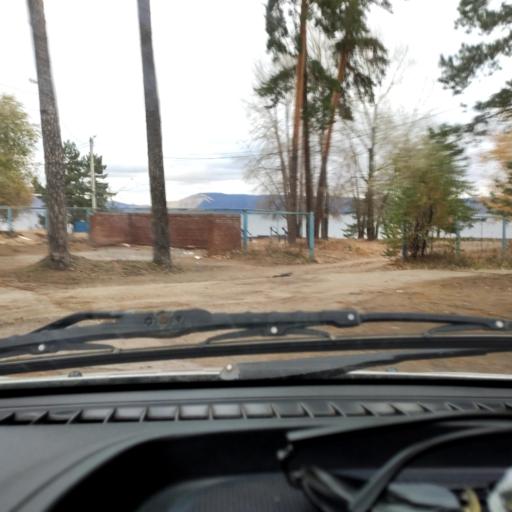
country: RU
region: Samara
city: Tol'yatti
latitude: 53.4743
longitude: 49.3339
